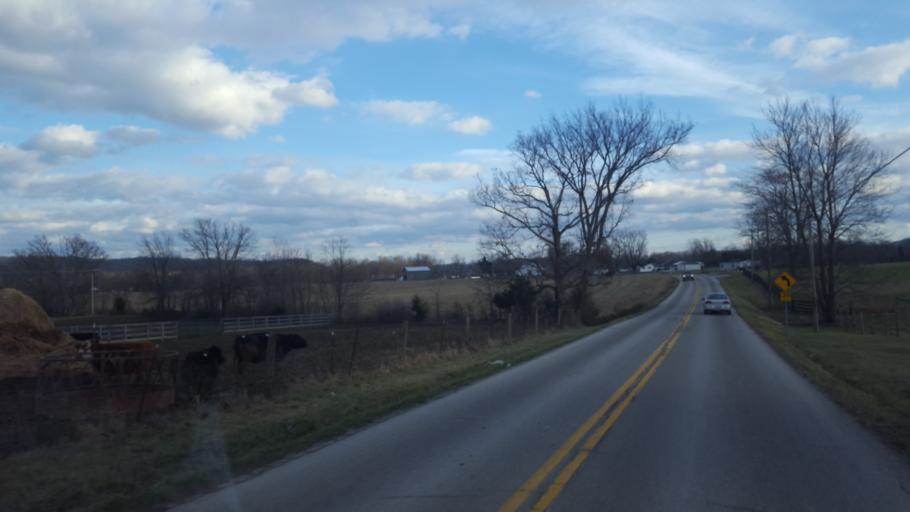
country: US
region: Kentucky
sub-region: Fleming County
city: Flemingsburg
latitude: 38.4807
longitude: -83.6075
